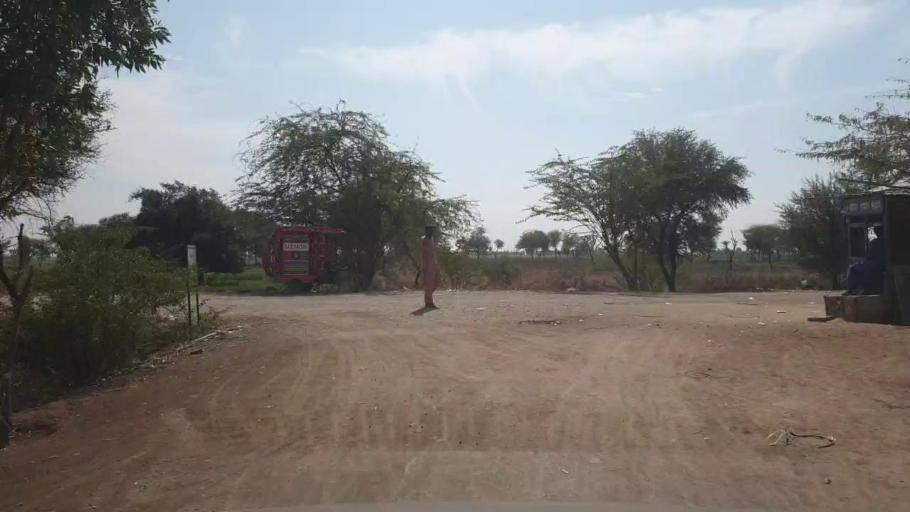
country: PK
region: Sindh
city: Mirwah Gorchani
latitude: 25.4317
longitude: 69.1964
